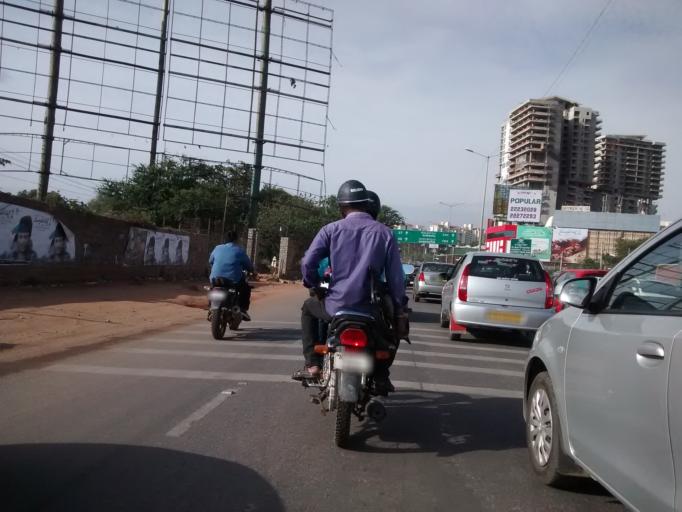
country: IN
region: Karnataka
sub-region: Bangalore Urban
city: Yelahanka
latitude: 13.0473
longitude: 77.5917
